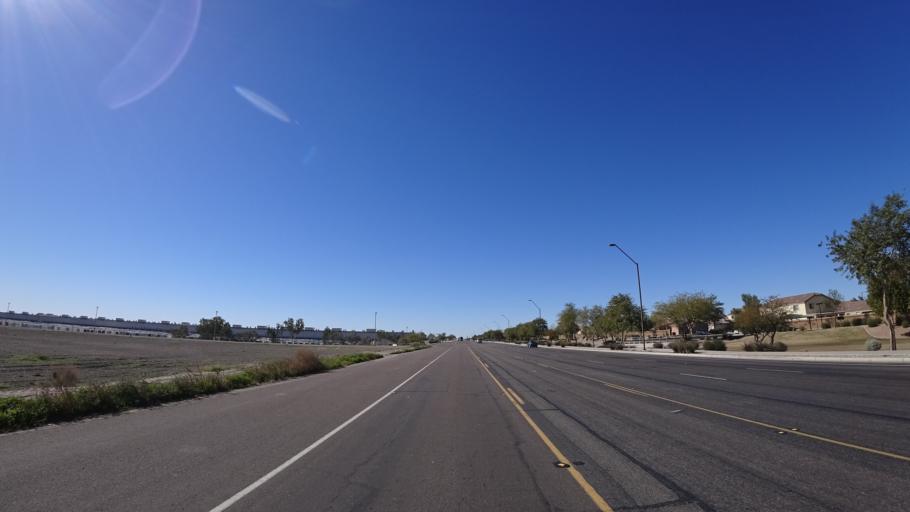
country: US
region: Arizona
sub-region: Maricopa County
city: Buckeye
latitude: 33.3921
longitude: -112.5583
